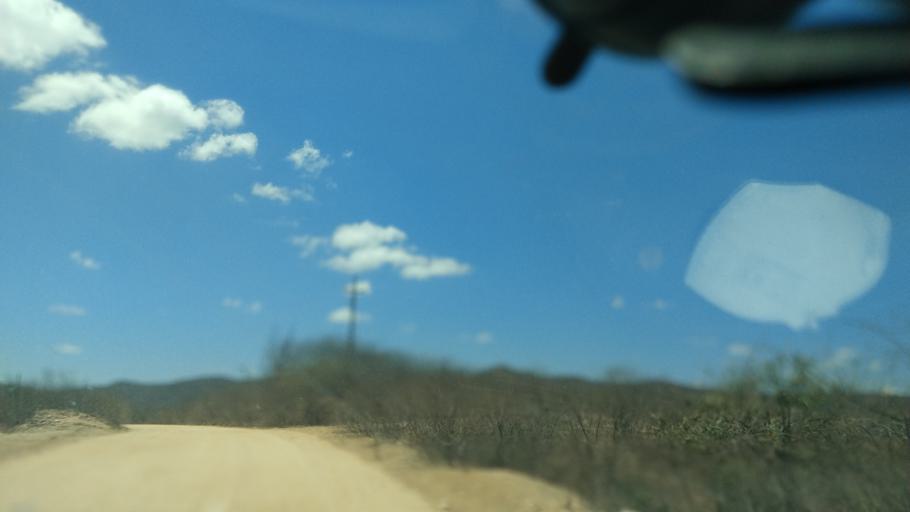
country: BR
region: Rio Grande do Norte
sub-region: Cerro Cora
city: Cerro Cora
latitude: -6.0148
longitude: -36.3048
